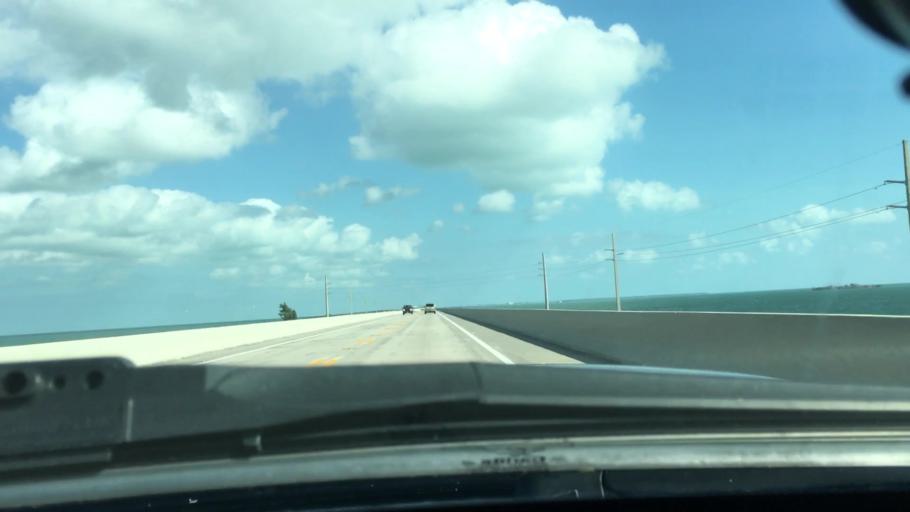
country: US
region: Florida
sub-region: Monroe County
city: Marathon
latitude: 24.6878
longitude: -81.2090
